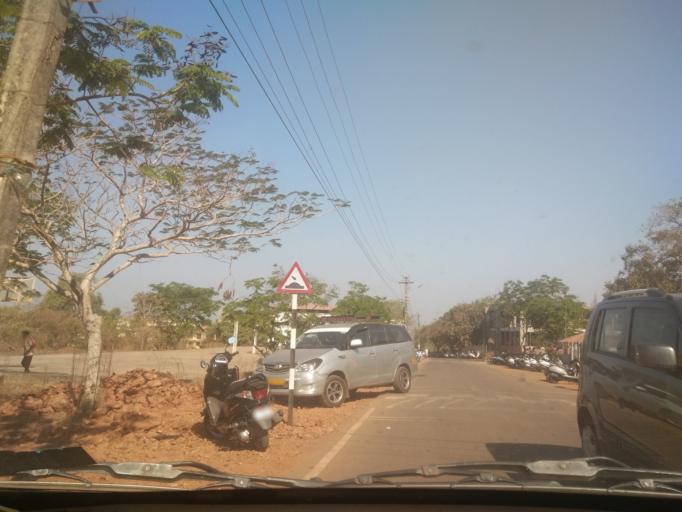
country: IN
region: Goa
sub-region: South Goa
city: Chicalim
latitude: 15.3920
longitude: 73.8634
